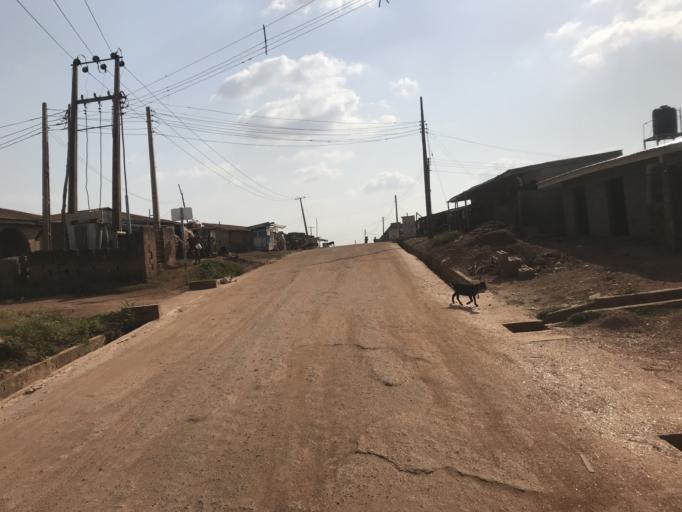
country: NG
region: Osun
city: Osogbo
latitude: 7.8085
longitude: 4.5583
